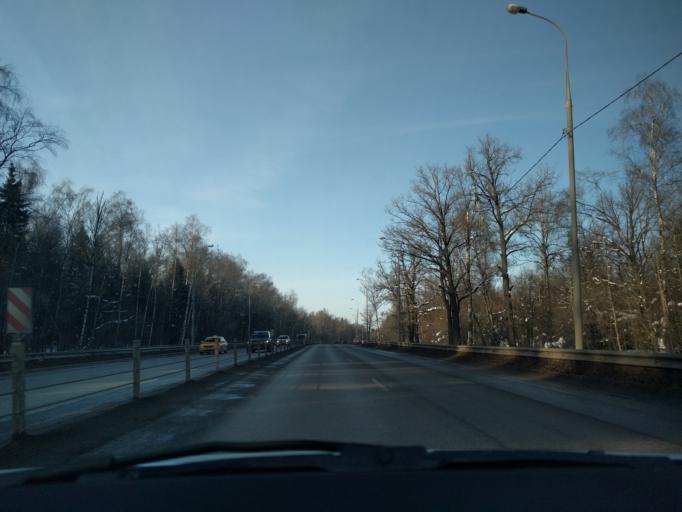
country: RU
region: Moskovskaya
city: Marfino
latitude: 56.0297
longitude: 37.5427
